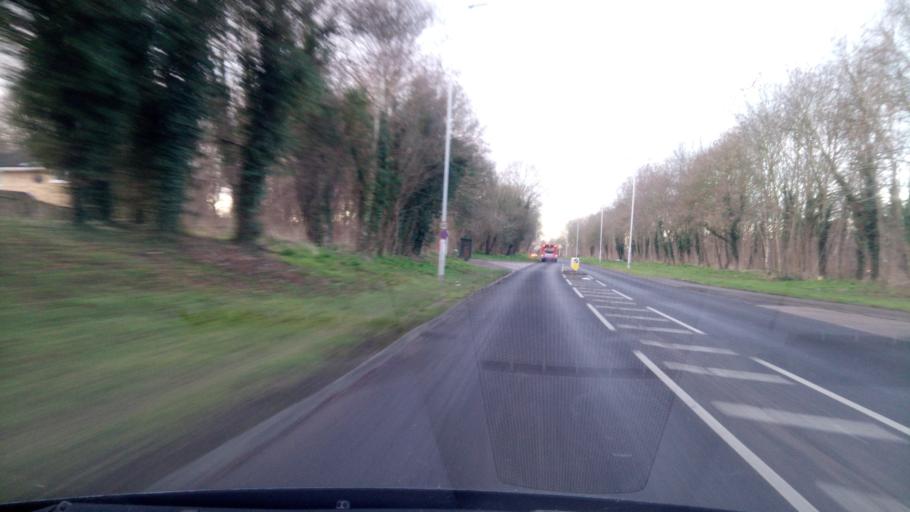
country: GB
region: England
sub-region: Peterborough
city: Marholm
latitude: 52.5858
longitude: -0.2867
